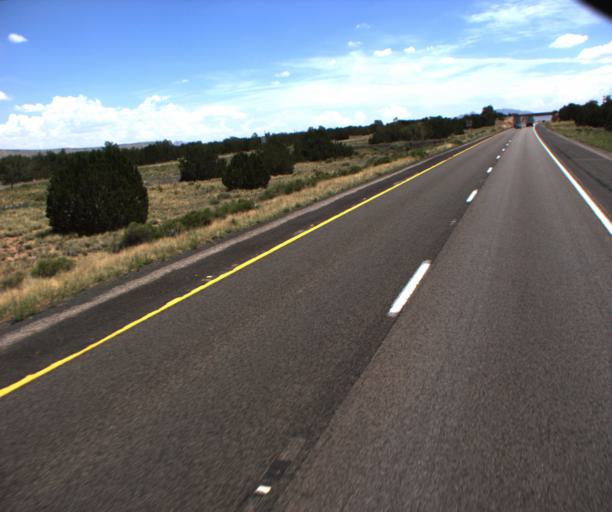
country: US
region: Arizona
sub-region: Mohave County
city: Peach Springs
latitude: 35.3182
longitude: -112.9545
